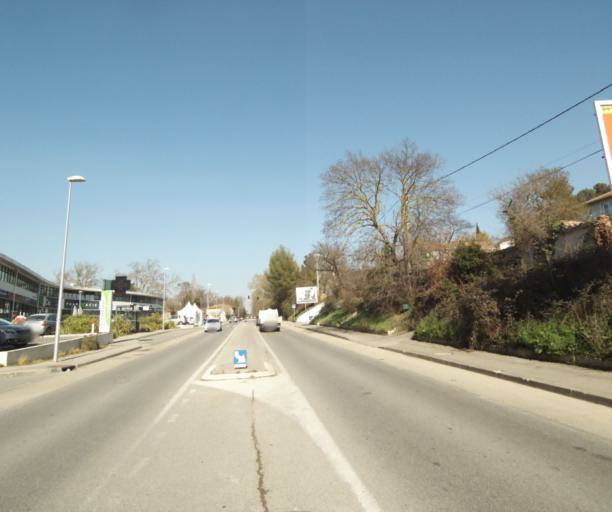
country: FR
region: Provence-Alpes-Cote d'Azur
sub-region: Departement des Bouches-du-Rhone
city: Bouc-Bel-Air
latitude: 43.4515
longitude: 5.3997
